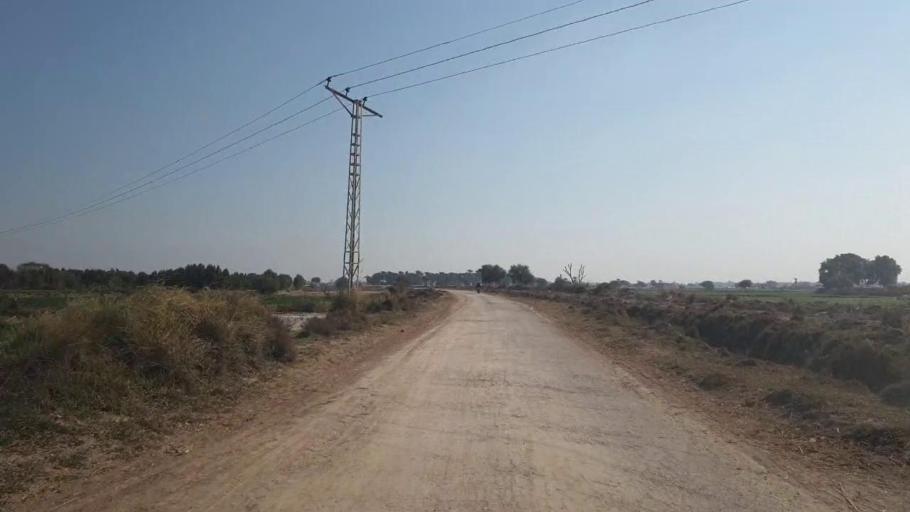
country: PK
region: Sindh
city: Shahdadpur
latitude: 25.9438
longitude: 68.6367
